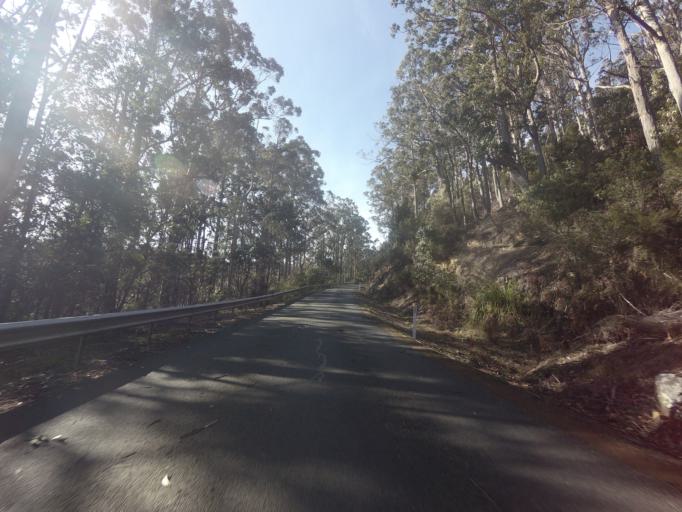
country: AU
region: Tasmania
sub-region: Kingborough
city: Kettering
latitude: -43.1683
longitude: 147.1839
